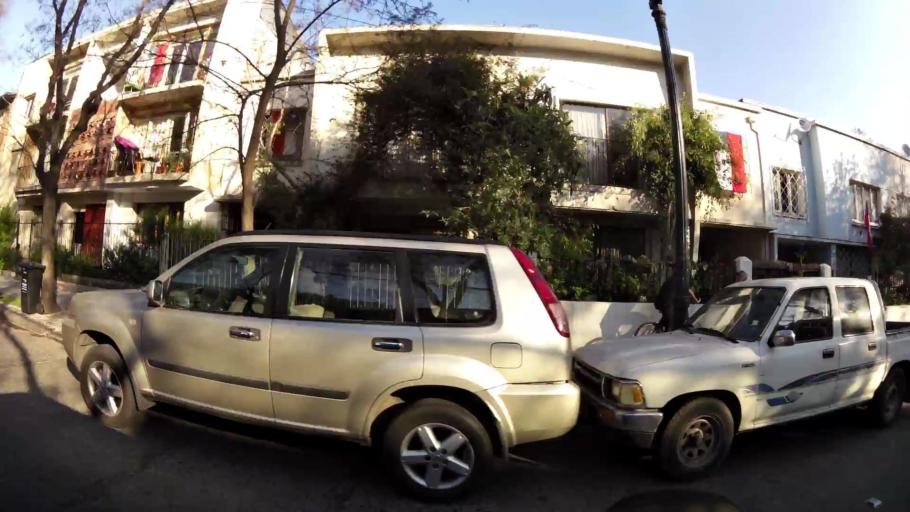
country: CL
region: Santiago Metropolitan
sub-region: Provincia de Santiago
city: Santiago
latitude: -33.4314
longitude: -70.6325
